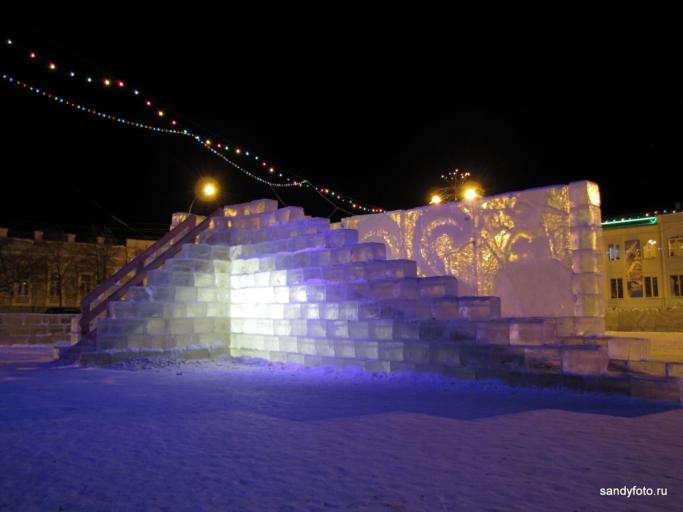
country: RU
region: Chelyabinsk
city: Troitsk
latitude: 54.0827
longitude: 61.5587
